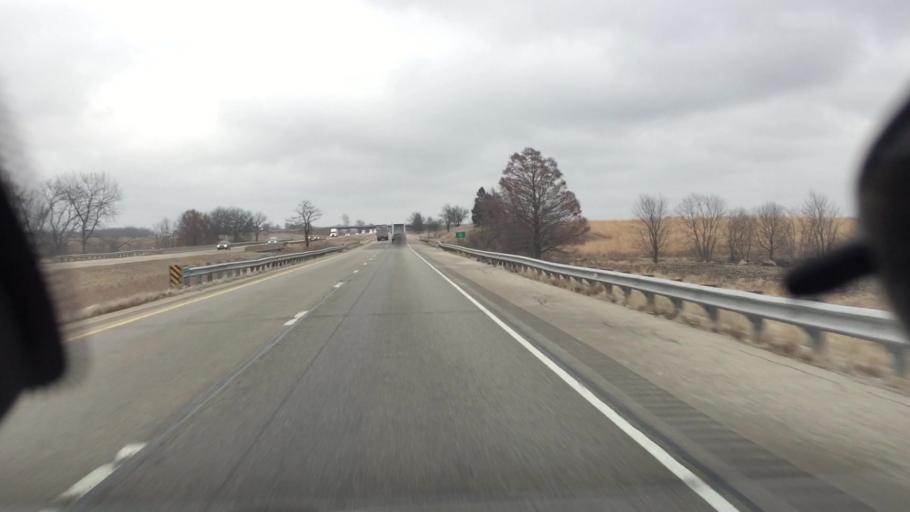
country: US
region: Illinois
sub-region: Tazewell County
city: Mackinaw
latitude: 40.6224
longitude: -89.3546
